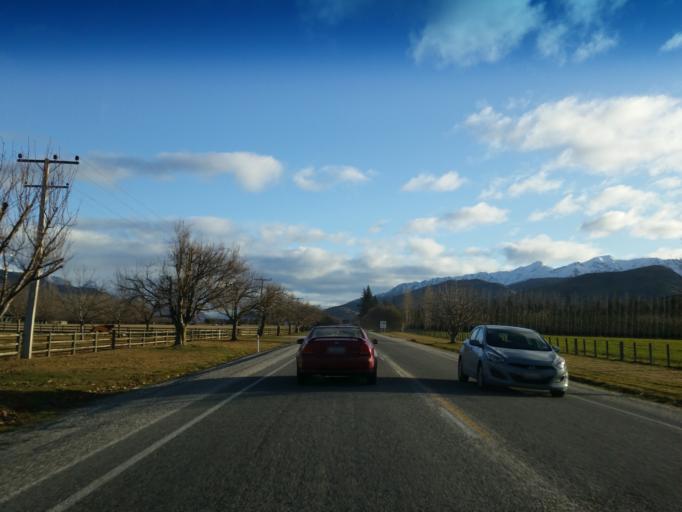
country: NZ
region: Otago
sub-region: Queenstown-Lakes District
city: Arrowtown
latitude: -44.9957
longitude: 168.7899
